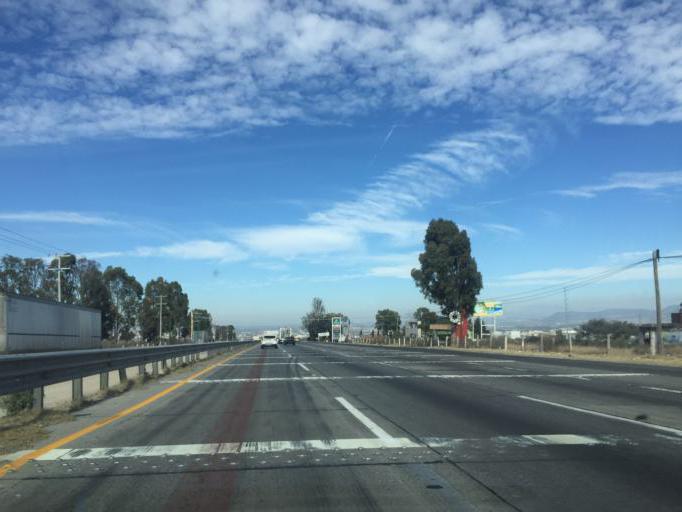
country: MX
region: Queretaro
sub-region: San Juan del Rio
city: Paso de Mata
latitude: 20.3581
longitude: -99.9610
